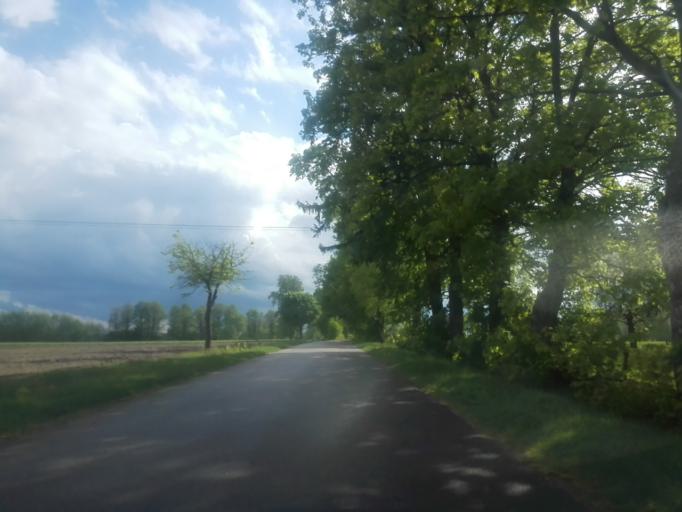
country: PL
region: Podlasie
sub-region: Powiat lomzynski
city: Wizna
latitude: 53.2311
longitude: 22.4239
